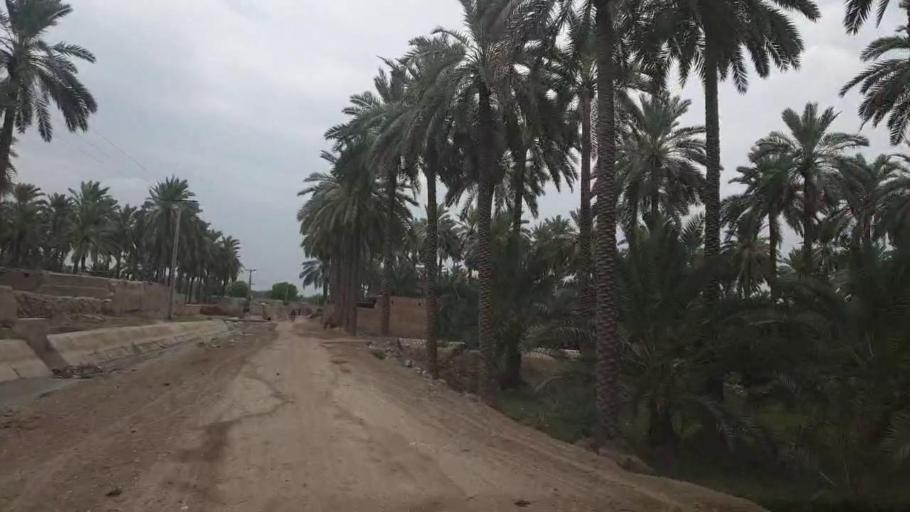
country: PK
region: Sindh
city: Khairpur
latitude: 27.6065
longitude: 68.8034
